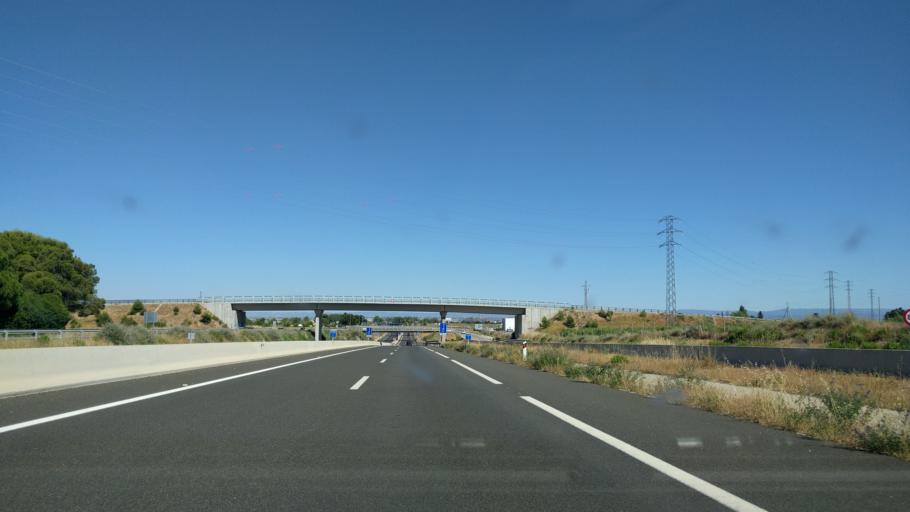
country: ES
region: Catalonia
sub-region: Provincia de Lleida
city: Alpicat
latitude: 41.6505
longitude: 0.5549
